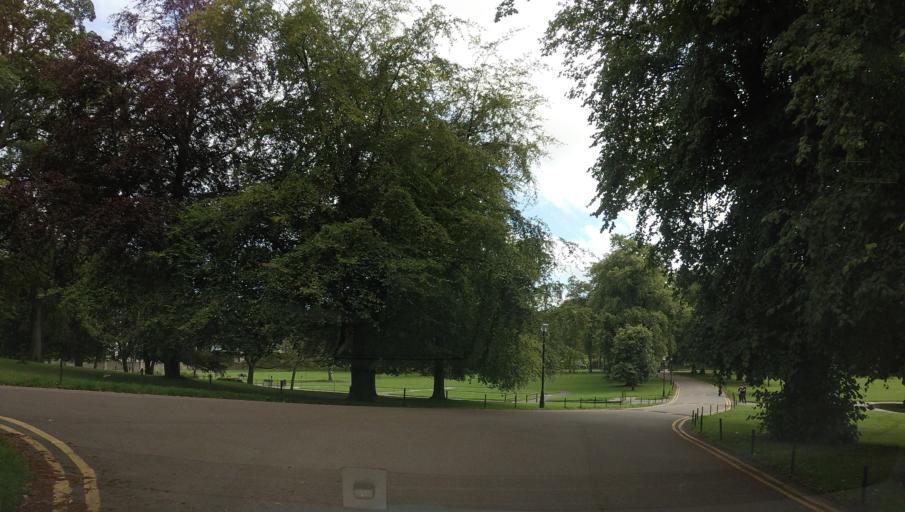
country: GB
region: Scotland
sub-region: Aberdeen City
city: Aberdeen
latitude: 57.1540
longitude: -2.1233
